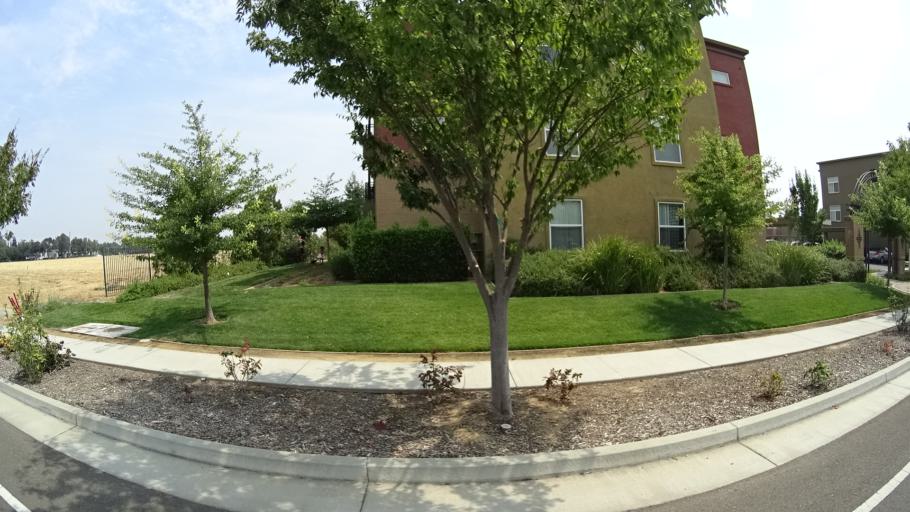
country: US
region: California
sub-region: Sacramento County
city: Laguna
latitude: 38.4072
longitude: -121.4090
